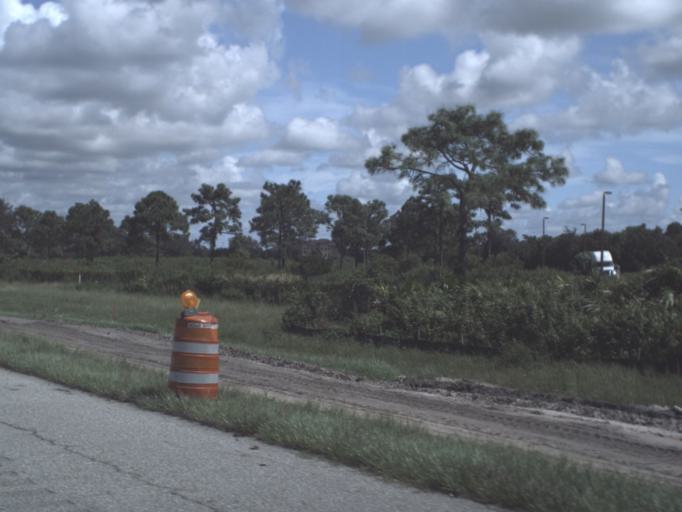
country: US
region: Florida
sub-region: Sarasota County
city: The Meadows
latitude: 27.3762
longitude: -82.4457
